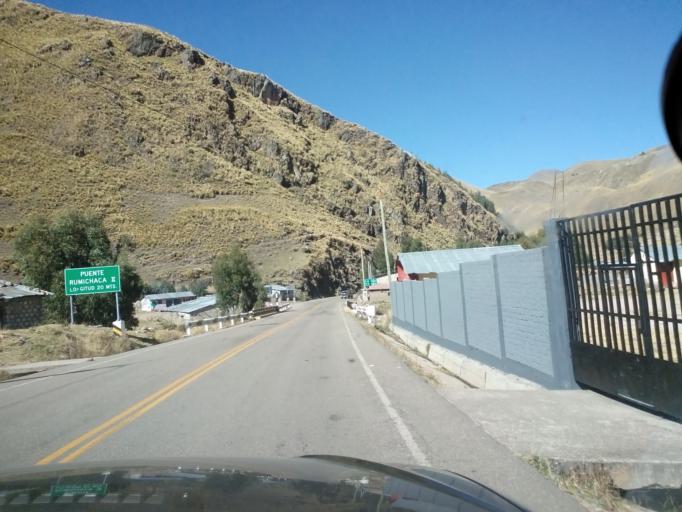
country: PE
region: Ayacucho
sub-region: Provincia de Huamanga
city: Vinchos
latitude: -13.3410
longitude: -74.5401
